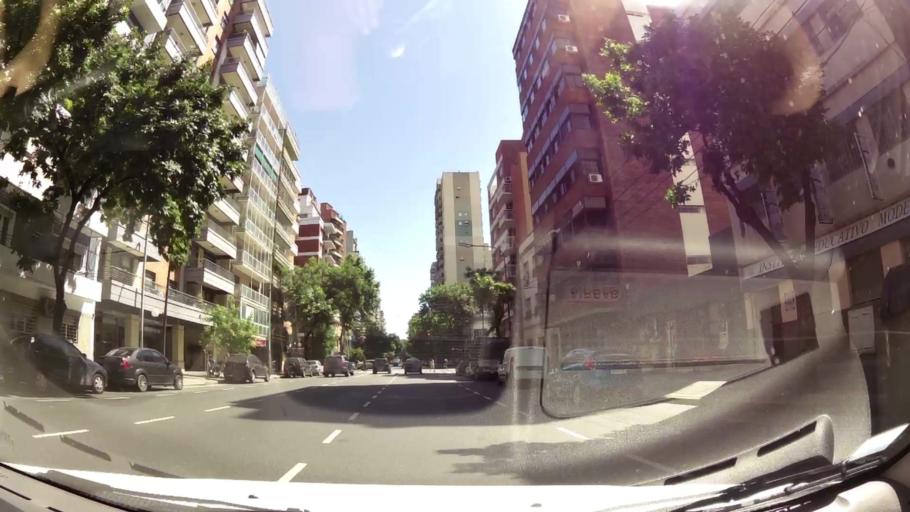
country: AR
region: Buenos Aires F.D.
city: Villa Santa Rita
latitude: -34.6267
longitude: -58.4504
